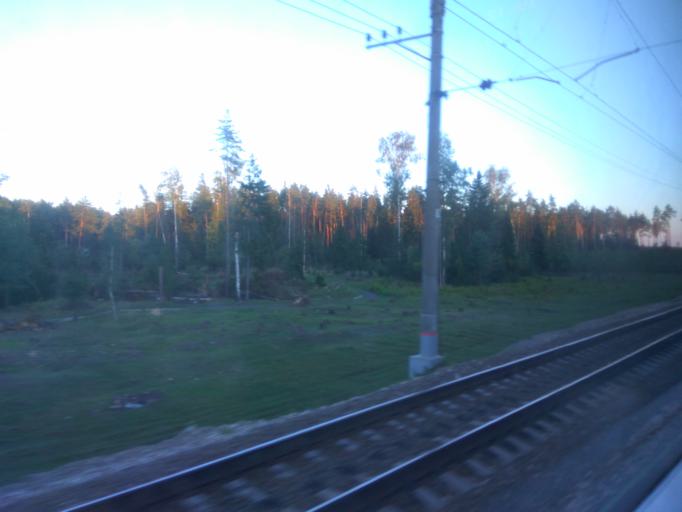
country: RU
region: Moskovskaya
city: Fryazevo
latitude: 55.7440
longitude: 38.4794
